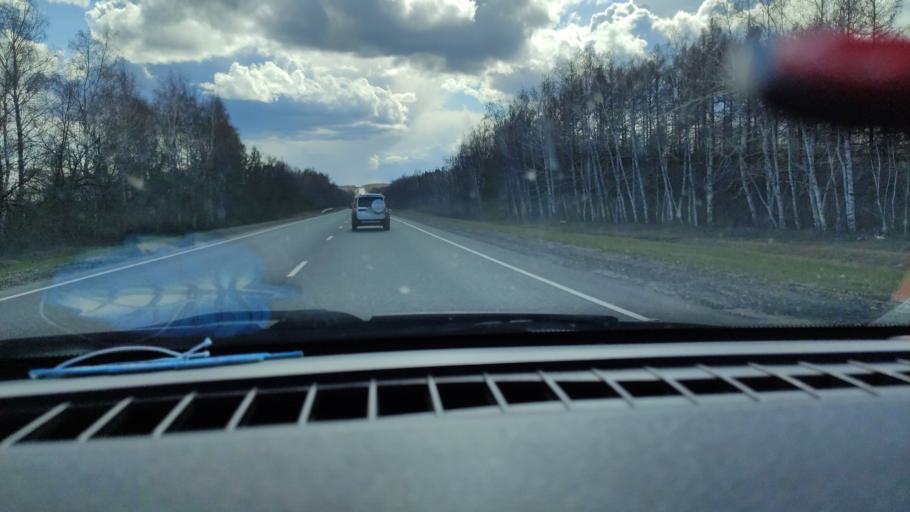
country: RU
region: Saratov
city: Khvalynsk
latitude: 52.5777
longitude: 48.1120
